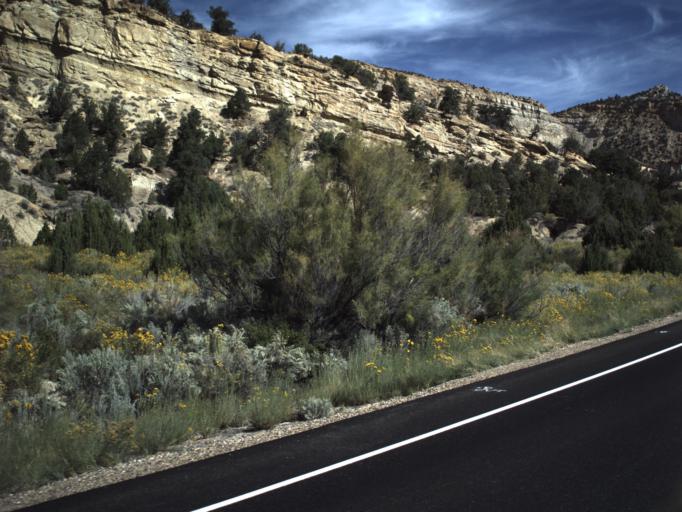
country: US
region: Utah
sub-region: Garfield County
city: Panguitch
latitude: 37.5954
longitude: -111.9219
